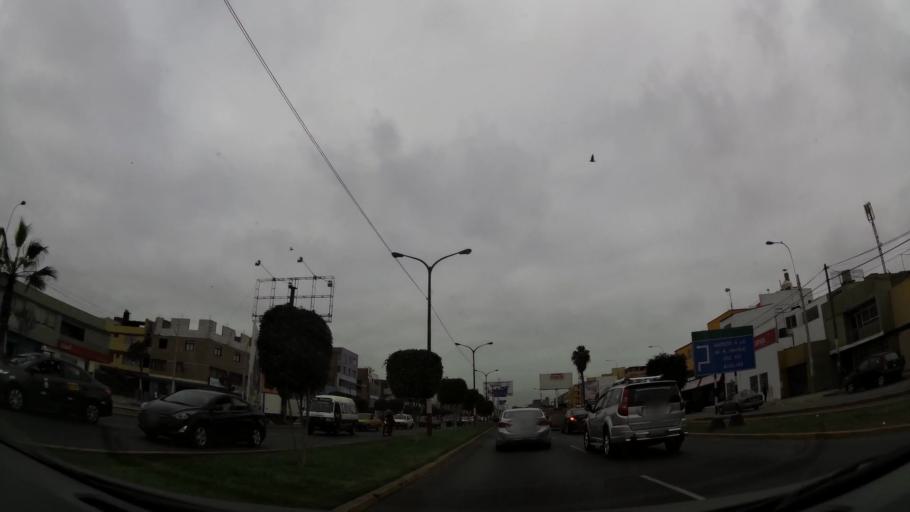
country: PE
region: Callao
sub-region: Callao
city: Callao
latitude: -12.0529
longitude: -77.0943
